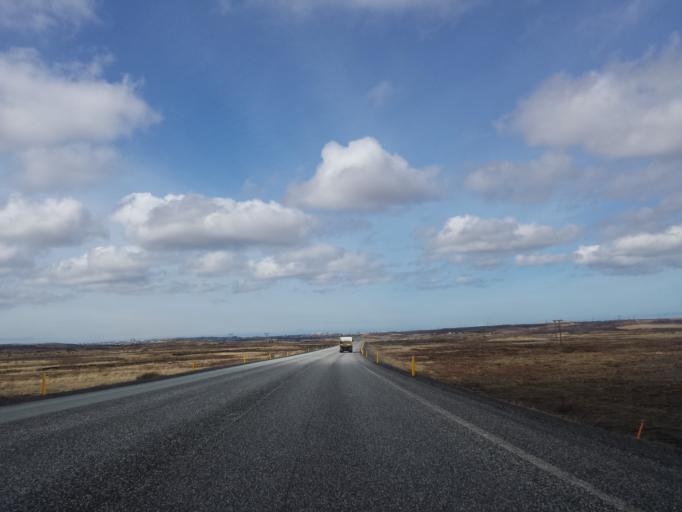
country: IS
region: Capital Region
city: Mosfellsbaer
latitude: 64.0734
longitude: -21.6379
